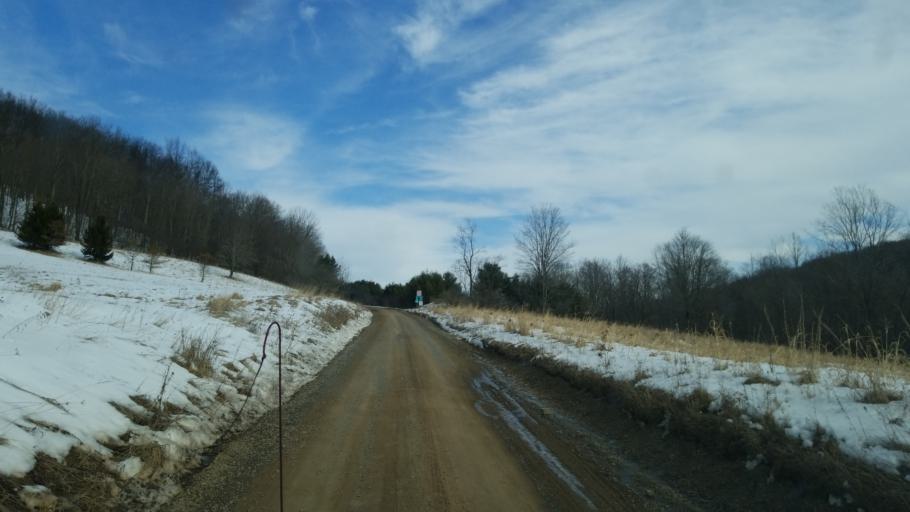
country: US
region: New York
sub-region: Allegany County
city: Andover
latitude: 41.9975
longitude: -77.8178
